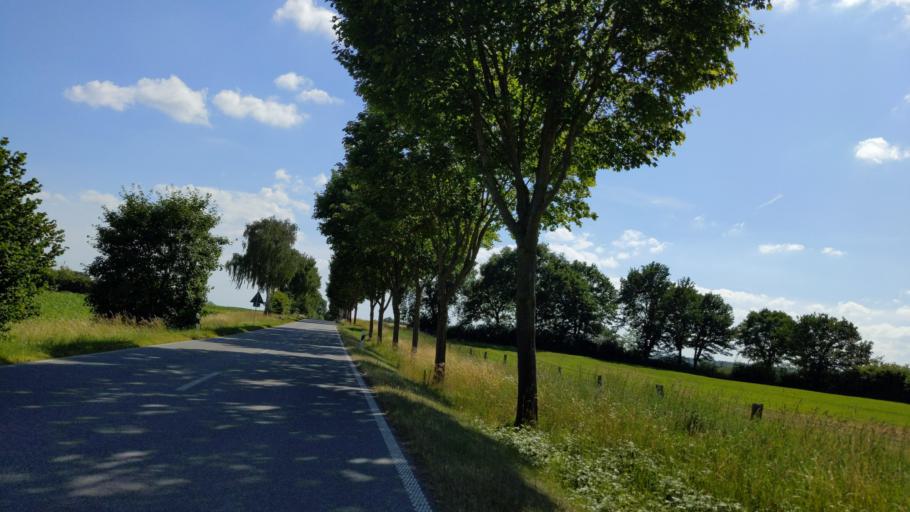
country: DE
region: Schleswig-Holstein
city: Berkenthin
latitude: 53.7223
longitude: 10.6503
